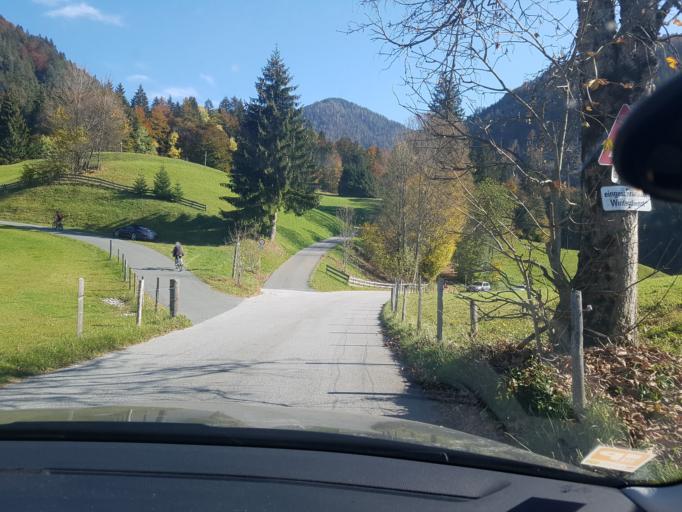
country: AT
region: Tyrol
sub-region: Politischer Bezirk Kitzbuhel
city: Hochfilzen
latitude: 47.5082
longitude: 12.5936
